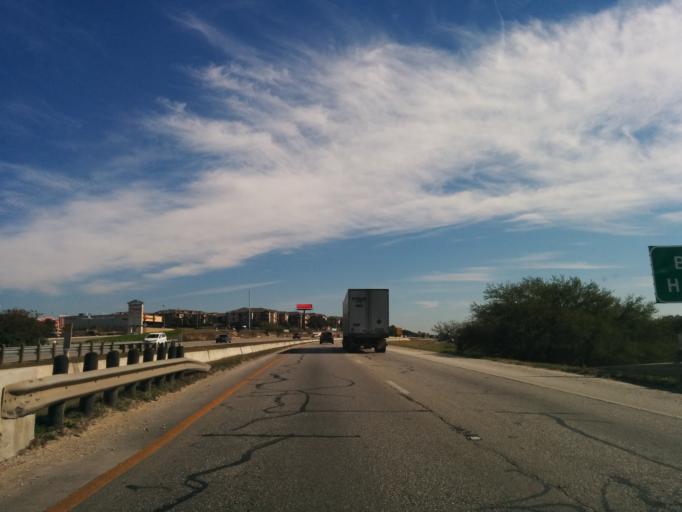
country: US
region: Texas
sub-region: Bexar County
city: Shavano Park
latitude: 29.5997
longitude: -98.5636
